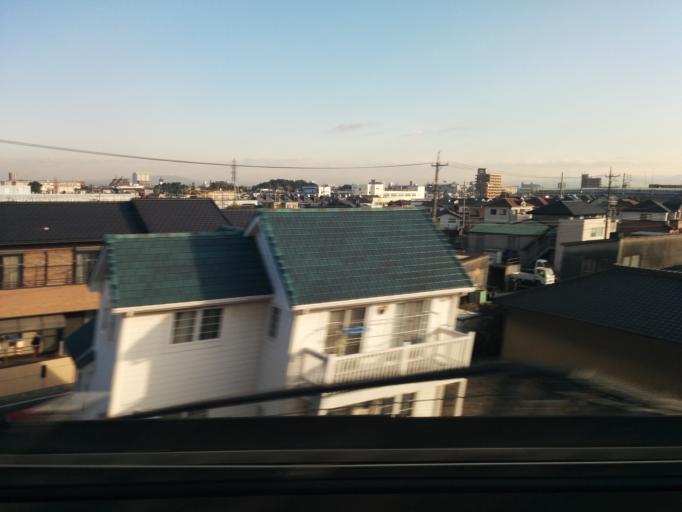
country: JP
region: Aichi
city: Chiryu
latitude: 34.9894
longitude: 137.0393
